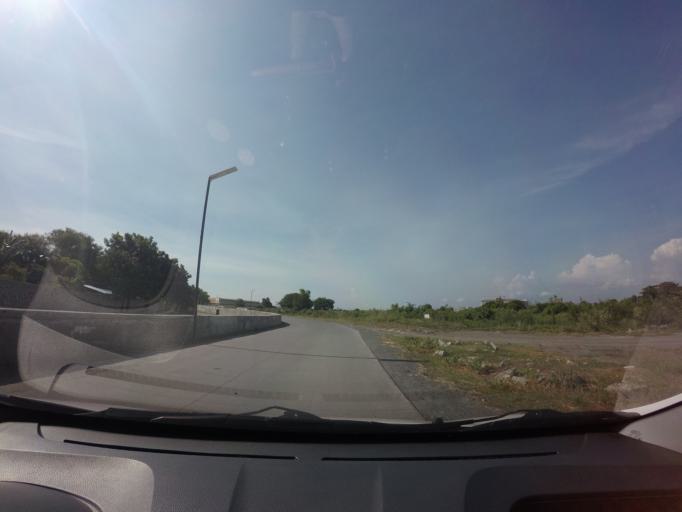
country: PH
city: Sambayanihan People's Village
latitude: 14.4719
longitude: 120.9863
